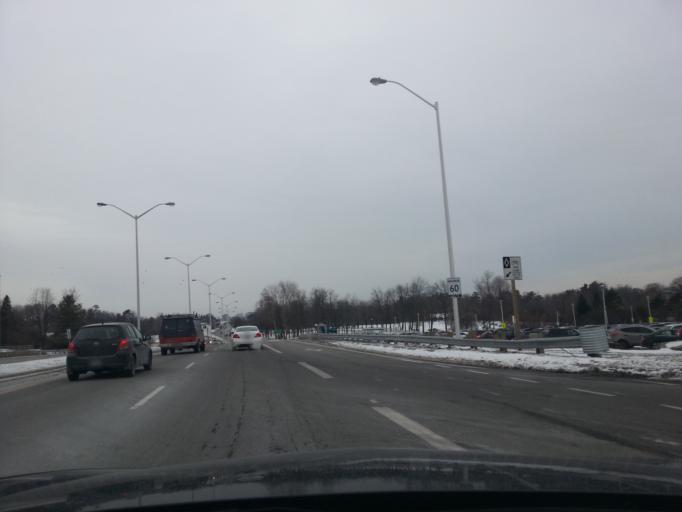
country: CA
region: Ontario
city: Ottawa
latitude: 45.3769
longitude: -75.6917
